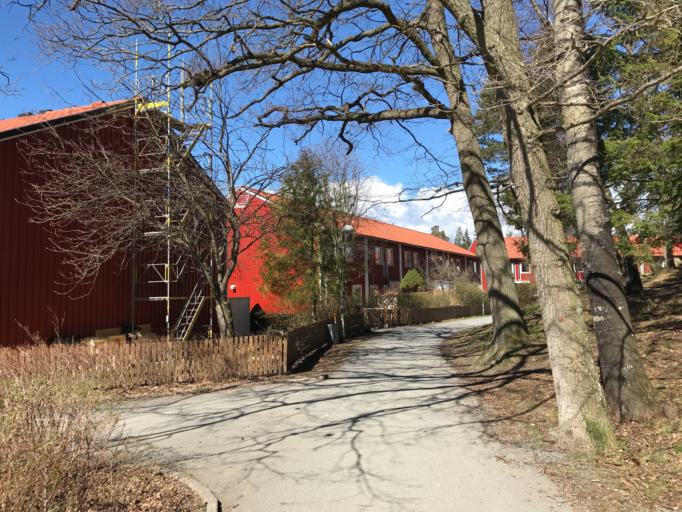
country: SE
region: Stockholm
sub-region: Stockholms Kommun
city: Kista
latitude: 59.4028
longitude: 17.9346
